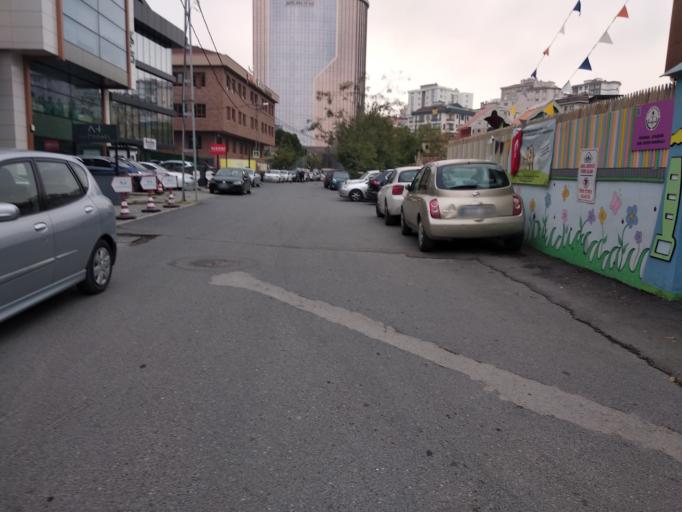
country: TR
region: Istanbul
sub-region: Atasehir
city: Atasehir
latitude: 40.9836
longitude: 29.1135
